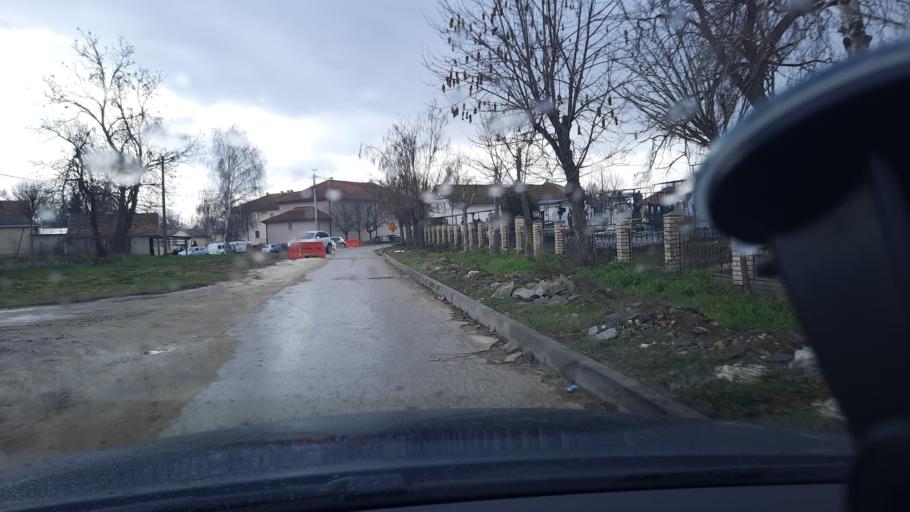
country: MK
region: Mogila
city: Mogila
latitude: 41.1088
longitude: 21.3793
